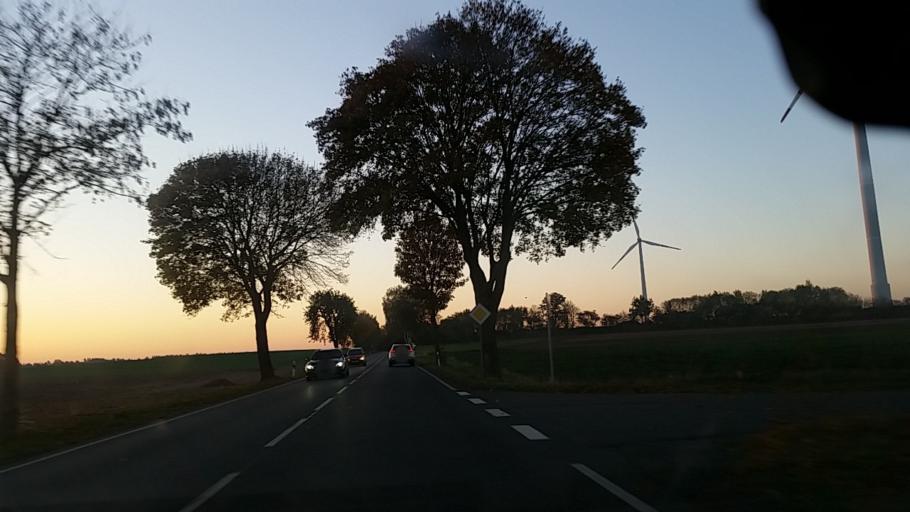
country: DE
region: Lower Saxony
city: Uelzen
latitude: 52.9425
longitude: 10.5914
